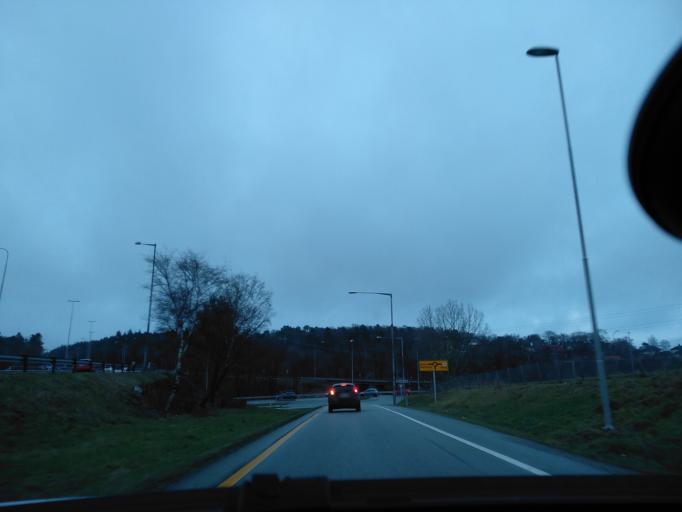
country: NO
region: Rogaland
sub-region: Stavanger
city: Stavanger
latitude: 58.9213
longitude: 5.7063
